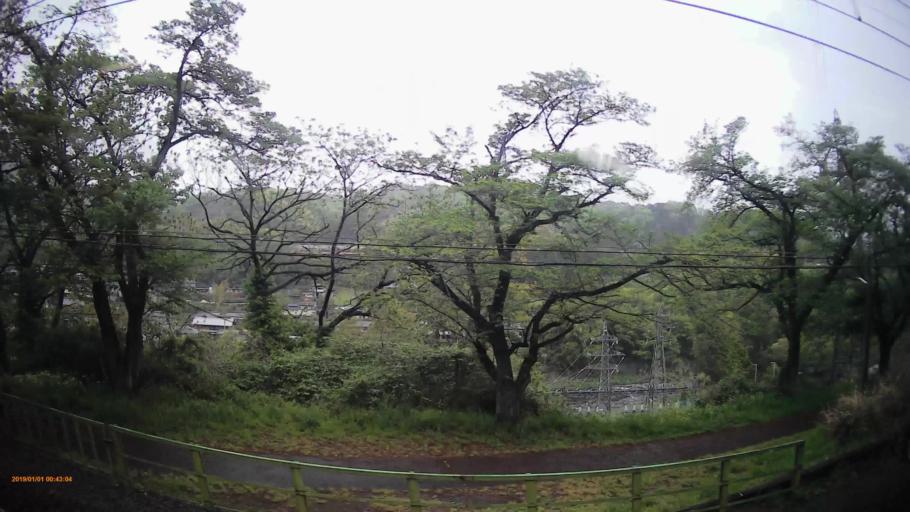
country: JP
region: Yamanashi
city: Otsuki
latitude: 35.6130
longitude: 138.9582
